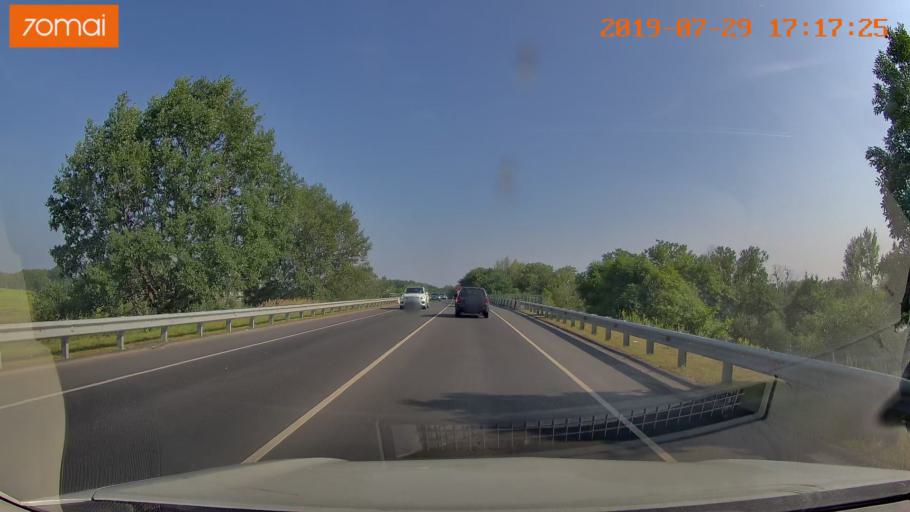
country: RU
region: Kaliningrad
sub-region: Gorod Kaliningrad
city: Kaliningrad
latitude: 54.7767
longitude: 20.4180
